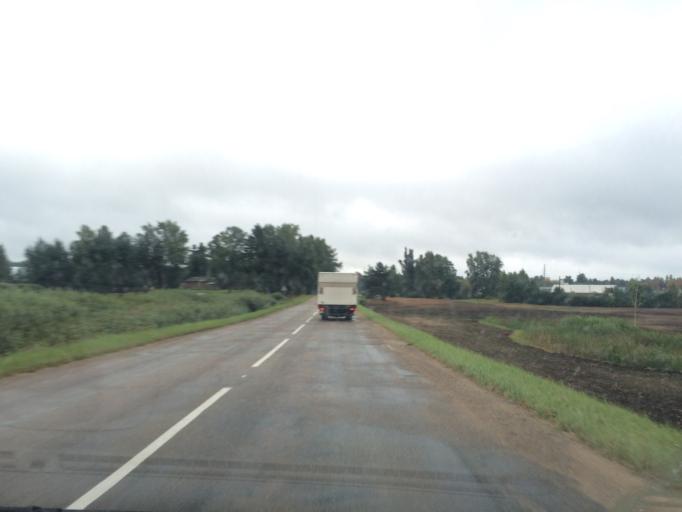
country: LV
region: Ikskile
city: Ikskile
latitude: 56.8497
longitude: 24.5035
